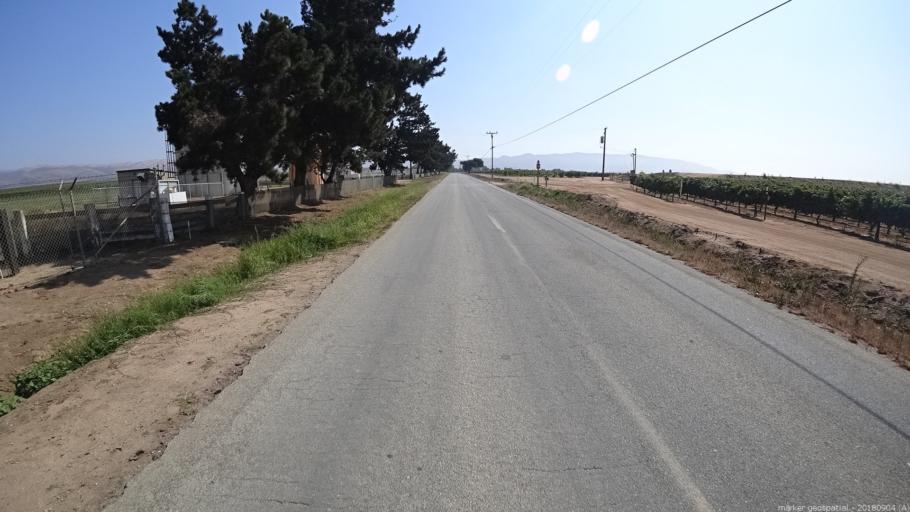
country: US
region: California
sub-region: Monterey County
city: Gonzales
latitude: 36.5028
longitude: -121.3900
